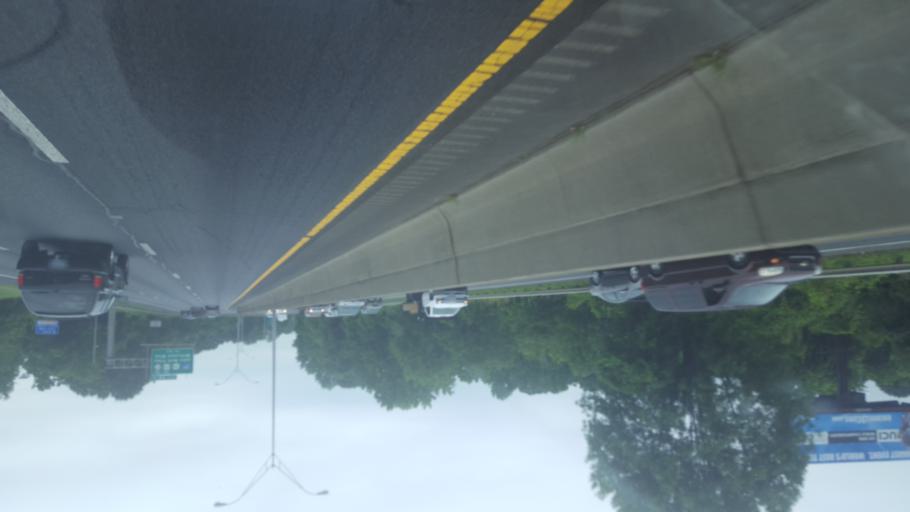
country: US
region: North Carolina
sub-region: Mecklenburg County
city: Charlotte
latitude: 35.2135
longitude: -80.8733
